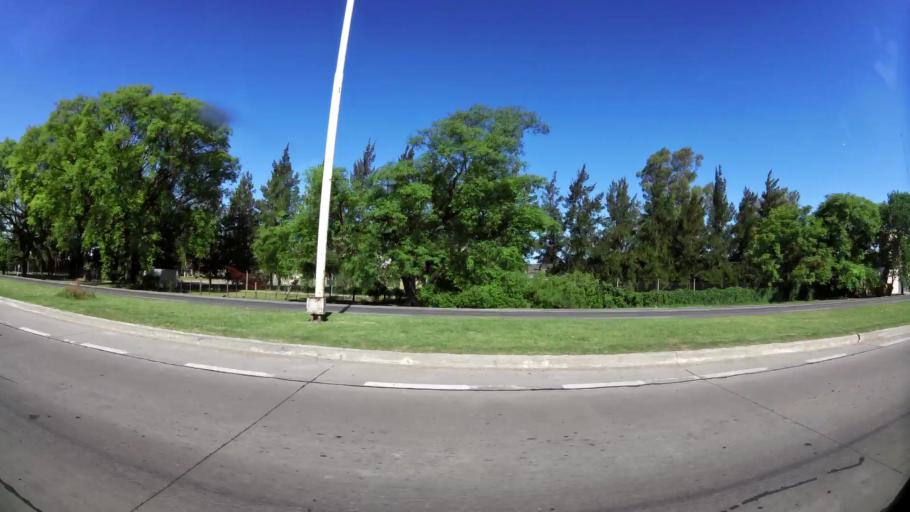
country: AR
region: Santa Fe
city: Rafaela
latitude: -31.2420
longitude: -61.5049
